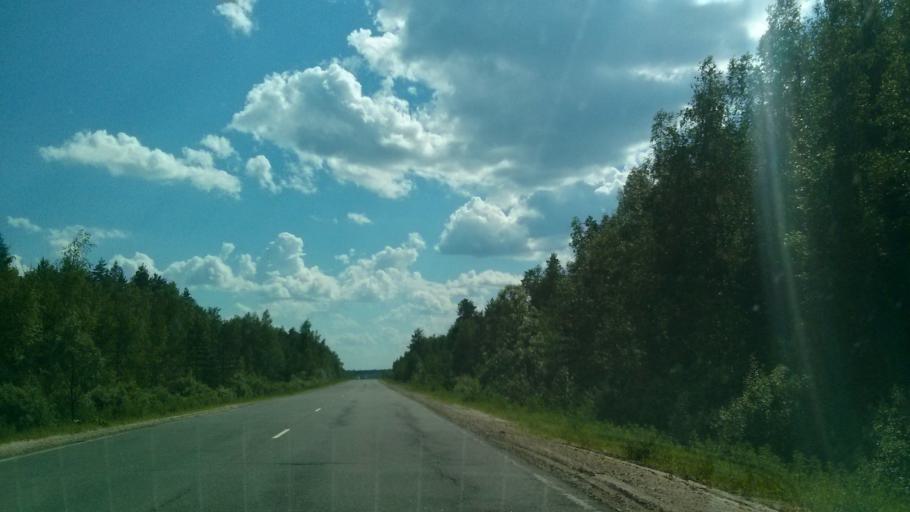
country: RU
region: Vladimir
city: Melenki
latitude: 55.3473
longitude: 41.6731
